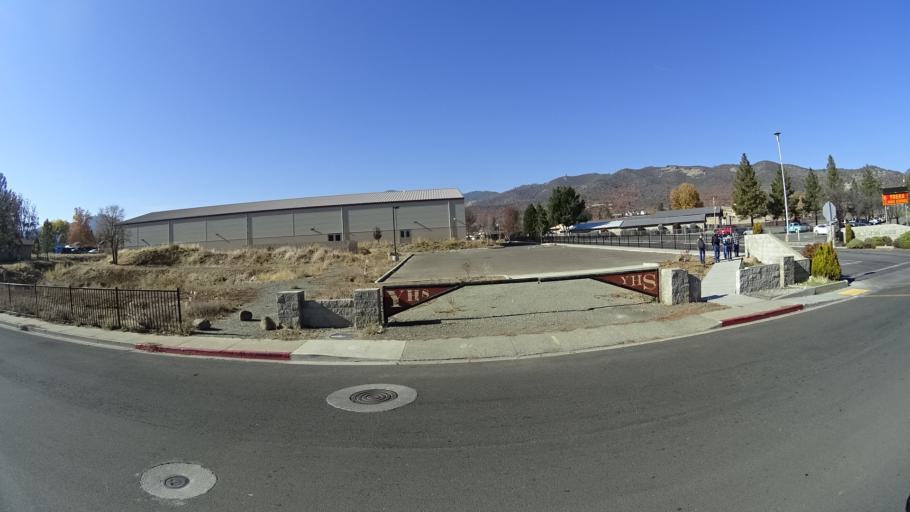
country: US
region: California
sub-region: Siskiyou County
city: Yreka
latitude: 41.7401
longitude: -122.6354
